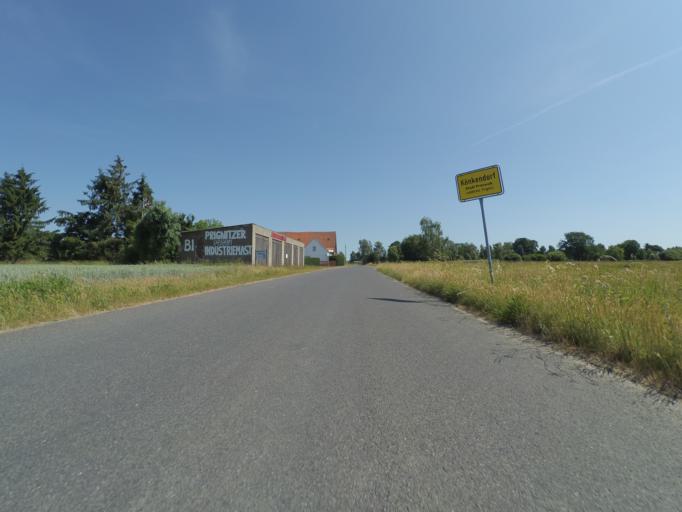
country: DE
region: Brandenburg
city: Heiligengrabe
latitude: 53.1820
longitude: 12.3025
